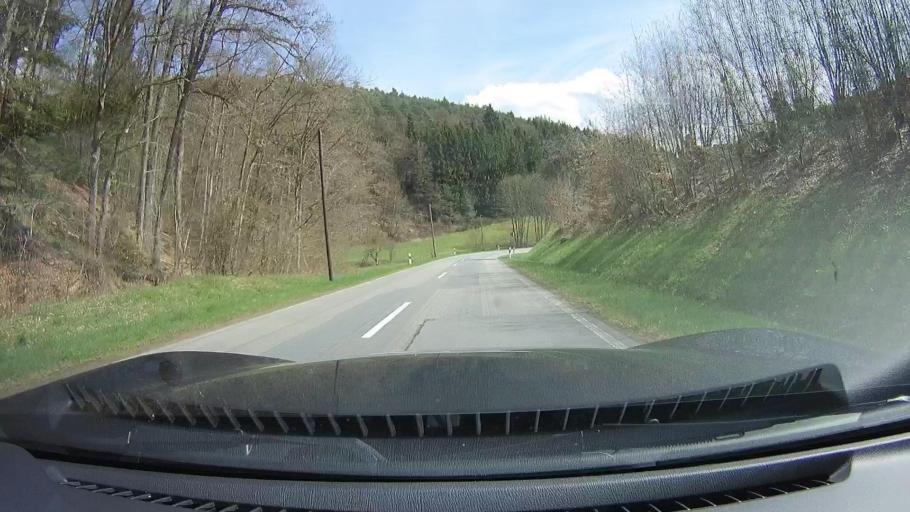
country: DE
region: Hesse
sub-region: Regierungsbezirk Darmstadt
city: Hesseneck
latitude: 49.5777
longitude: 9.0566
